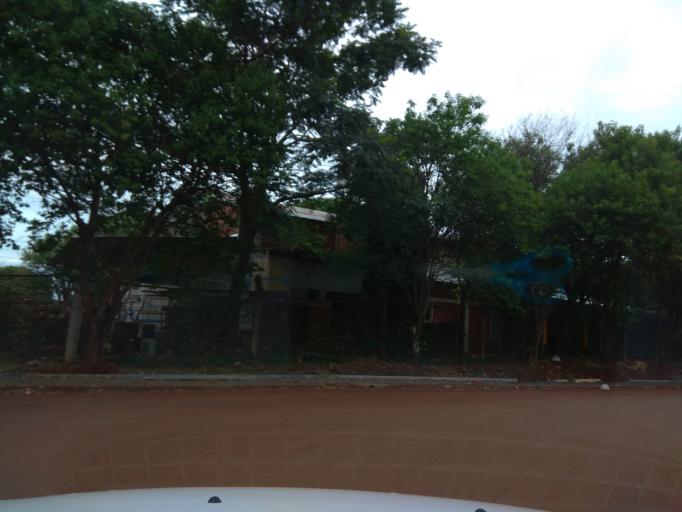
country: AR
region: Misiones
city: Garupa
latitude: -27.4451
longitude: -55.8695
